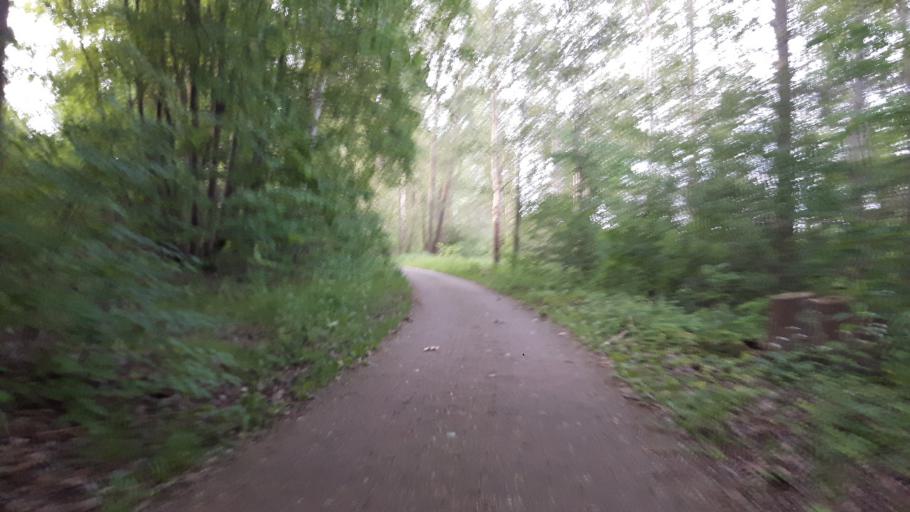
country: DE
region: Brandenburg
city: Gartz
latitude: 53.2199
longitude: 14.4063
